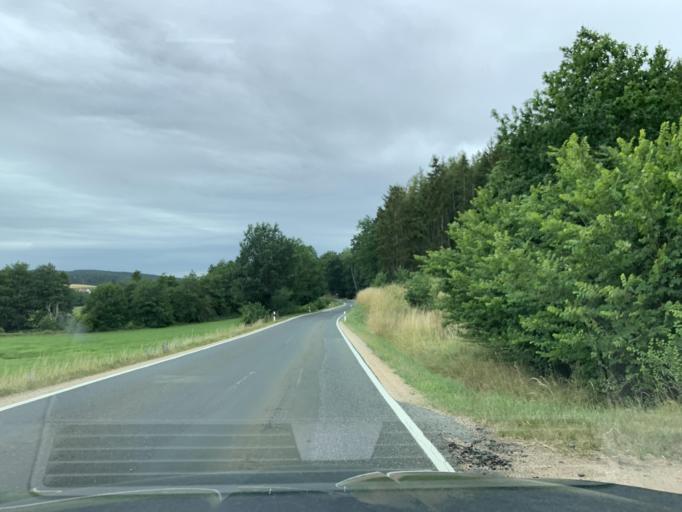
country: DE
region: Bavaria
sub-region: Upper Palatinate
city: Pettendorf
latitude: 49.3646
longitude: 12.3581
